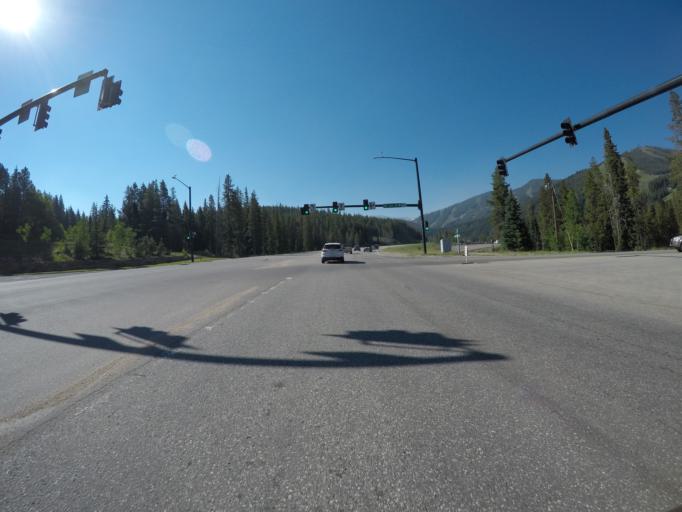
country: US
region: Colorado
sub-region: Grand County
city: Fraser
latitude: 39.8913
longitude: -105.7610
